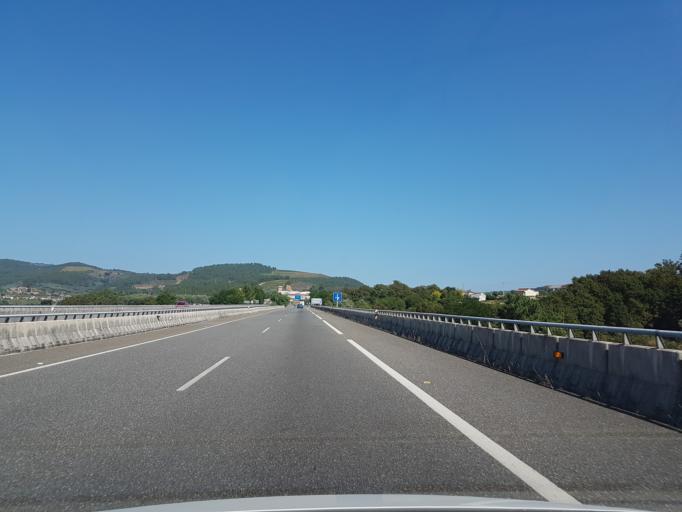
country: ES
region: Galicia
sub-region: Provincia de Ourense
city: Ribadavia
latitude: 42.3025
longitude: -8.1291
